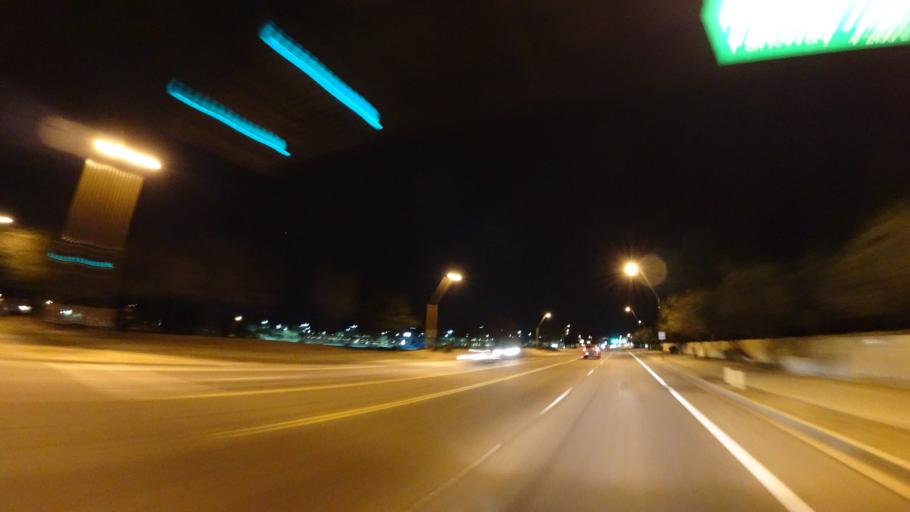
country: US
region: Arizona
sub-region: Maricopa County
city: San Carlos
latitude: 33.3347
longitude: -111.8976
